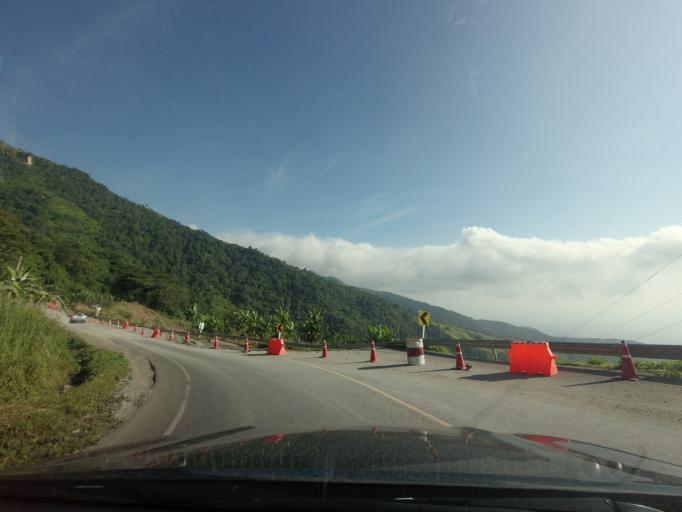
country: TH
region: Phetchabun
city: Lom Kao
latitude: 16.8838
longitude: 101.1174
